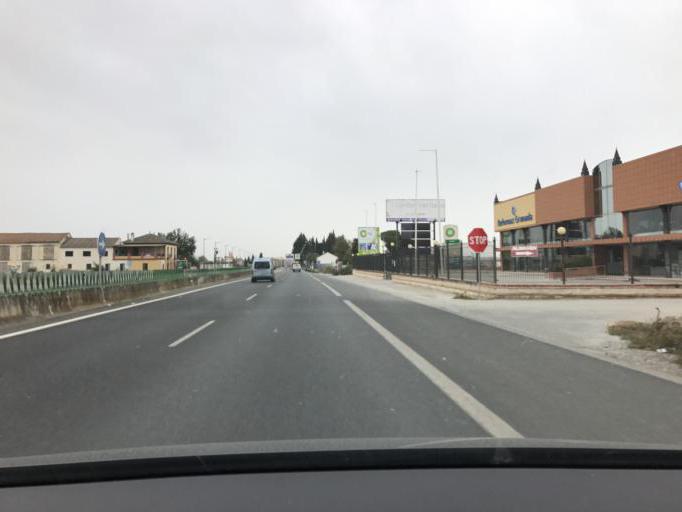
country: ES
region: Andalusia
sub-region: Provincia de Granada
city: Atarfe
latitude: 37.1932
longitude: -3.6998
